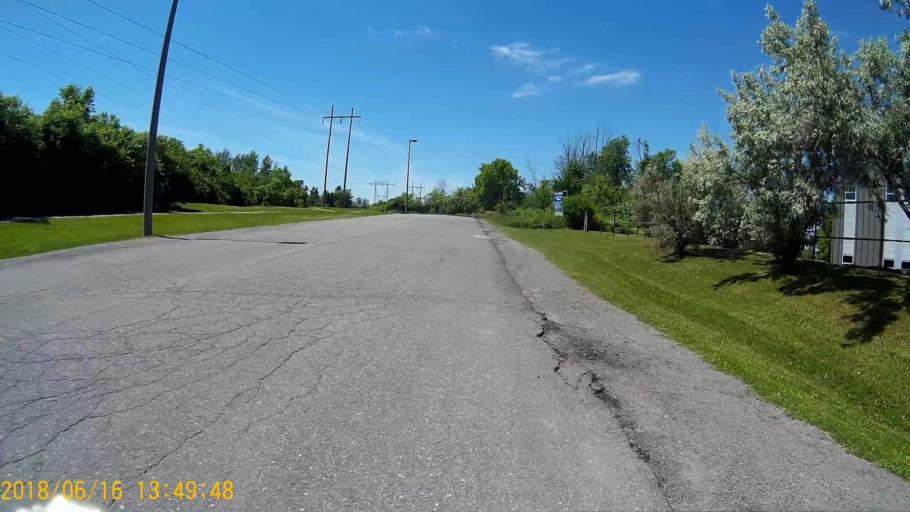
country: CA
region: Ontario
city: Bells Corners
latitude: 45.3357
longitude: -75.9128
